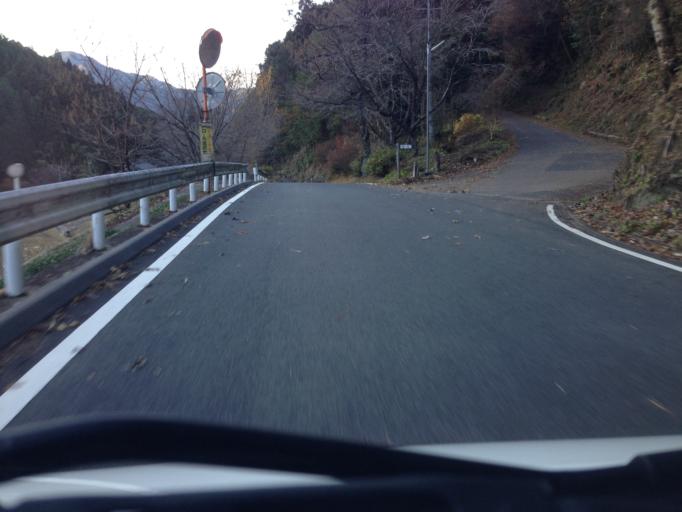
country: JP
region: Gifu
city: Mitake
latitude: 35.6058
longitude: 137.1950
